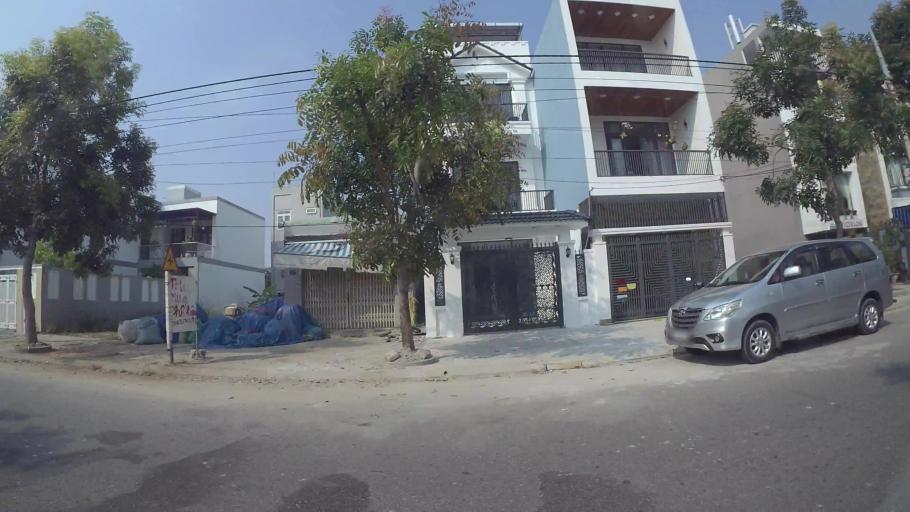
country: VN
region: Da Nang
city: Ngu Hanh Son
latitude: 16.0307
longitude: 108.2414
